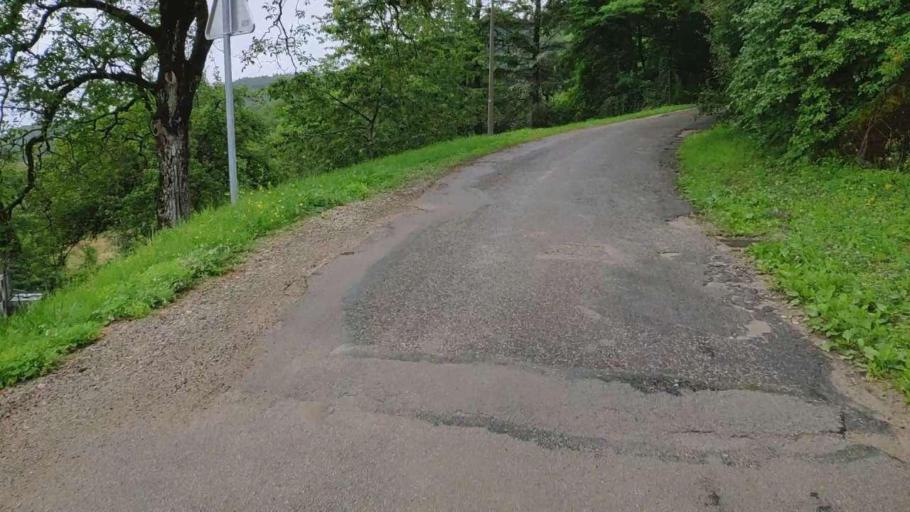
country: FR
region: Franche-Comte
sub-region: Departement du Jura
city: Poligny
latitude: 46.7870
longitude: 5.6178
